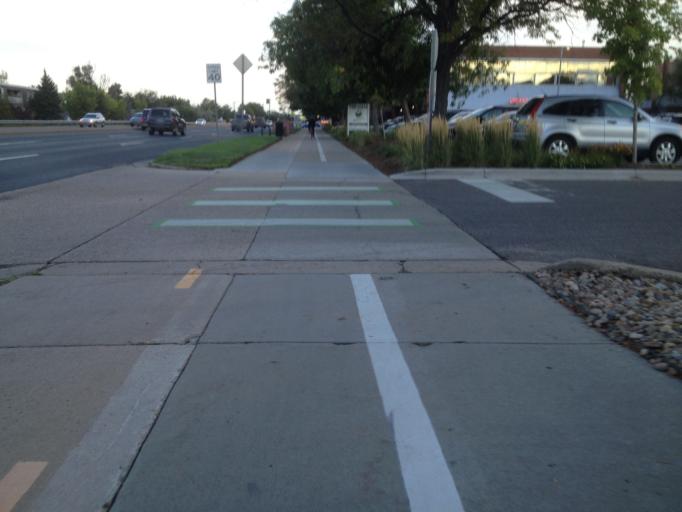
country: US
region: Colorado
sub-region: Boulder County
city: Boulder
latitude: 39.9851
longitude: -105.2497
